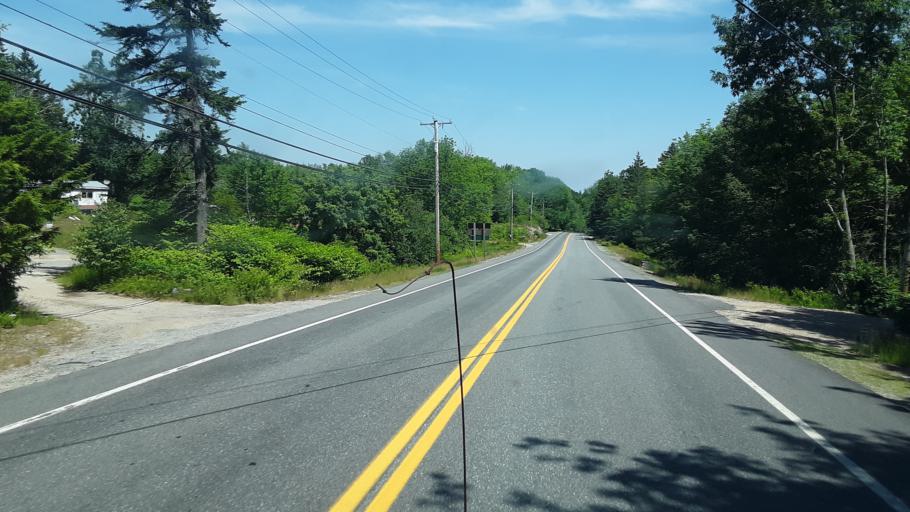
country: US
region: Maine
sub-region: Hancock County
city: Gouldsboro
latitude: 44.4699
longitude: -68.0875
